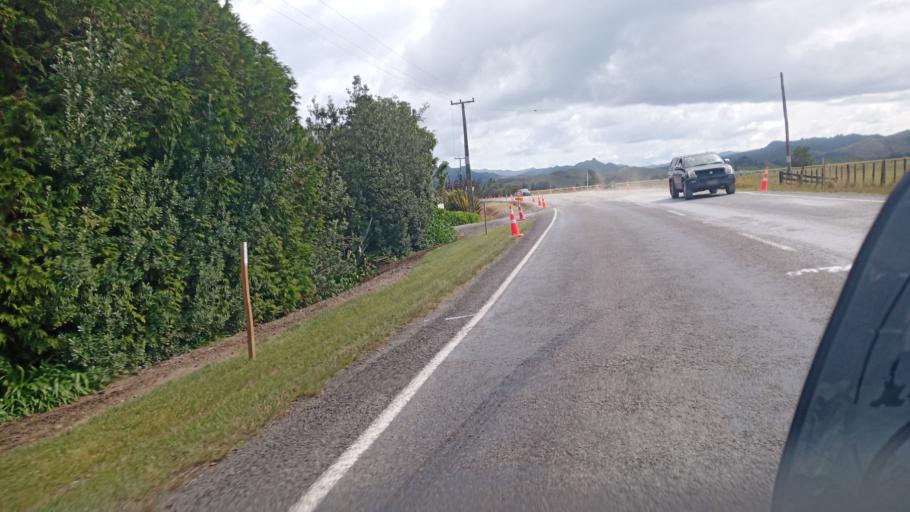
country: NZ
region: Gisborne
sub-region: Gisborne District
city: Gisborne
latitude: -38.3472
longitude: 178.3003
